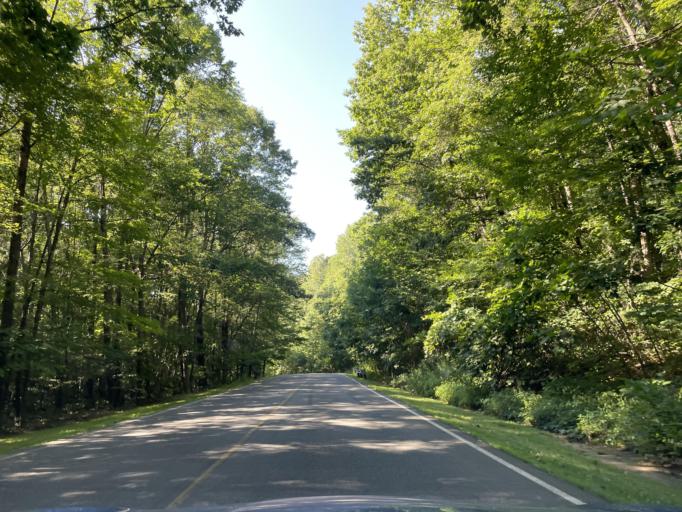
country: US
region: Massachusetts
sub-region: Worcester County
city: Sturbridge
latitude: 42.1450
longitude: -72.0489
